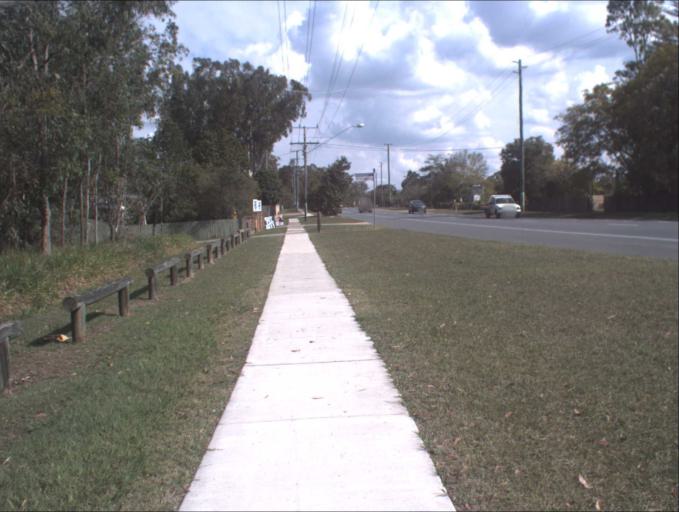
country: AU
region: Queensland
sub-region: Logan
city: Park Ridge South
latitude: -27.7000
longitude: 153.0108
